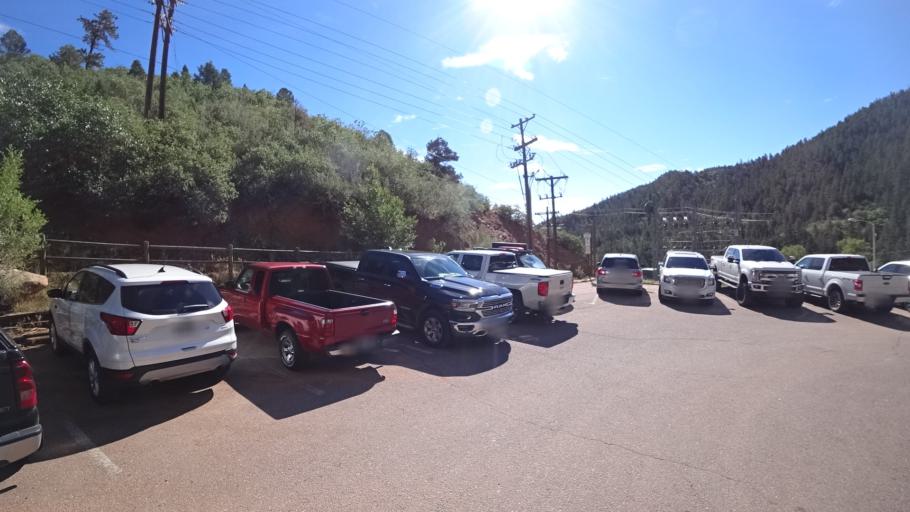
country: US
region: Colorado
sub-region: El Paso County
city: Manitou Springs
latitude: 38.8561
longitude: -104.9339
